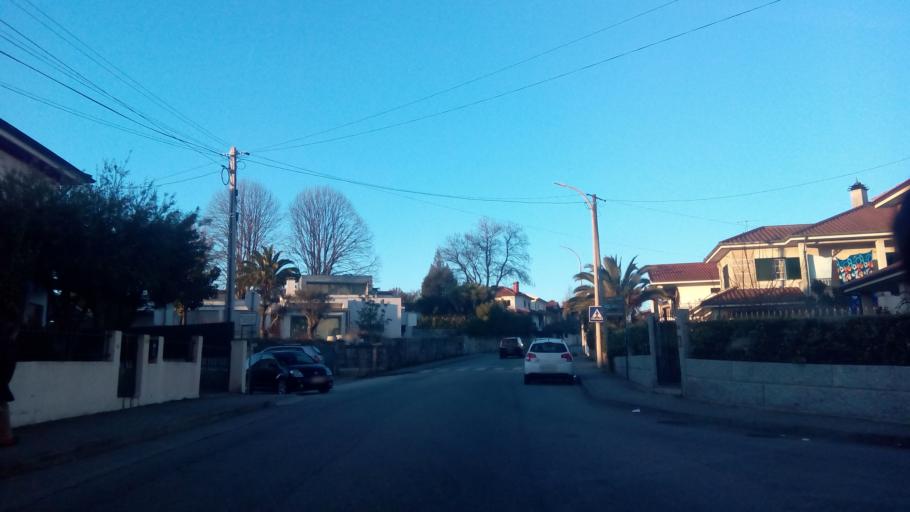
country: PT
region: Porto
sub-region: Amarante
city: Amarante
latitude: 41.2747
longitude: -8.0848
